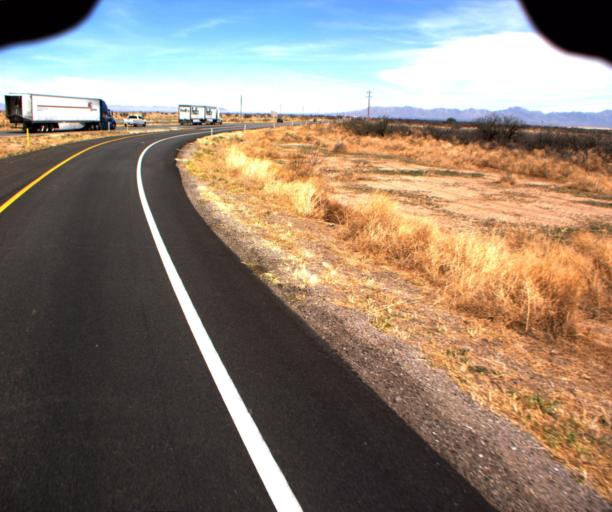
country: US
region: Arizona
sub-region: Cochise County
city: Willcox
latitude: 32.1771
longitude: -109.9474
